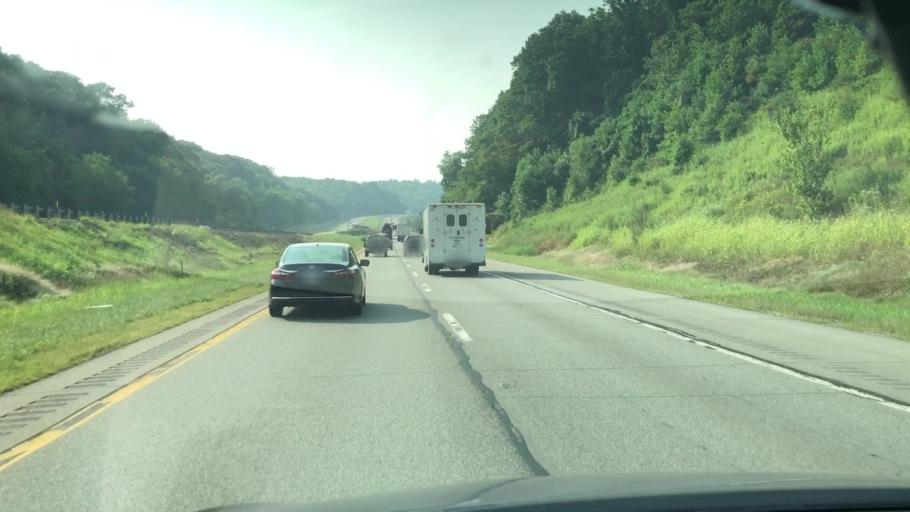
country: US
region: Pennsylvania
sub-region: Allegheny County
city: Franklin Park
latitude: 40.5791
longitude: -80.0961
